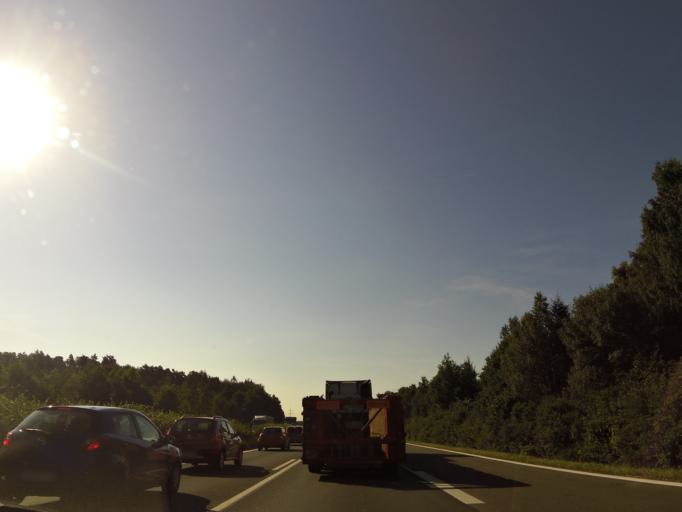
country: DE
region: Bavaria
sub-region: Regierungsbezirk Mittelfranken
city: Obermichelbach
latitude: 49.5675
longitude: 10.9417
